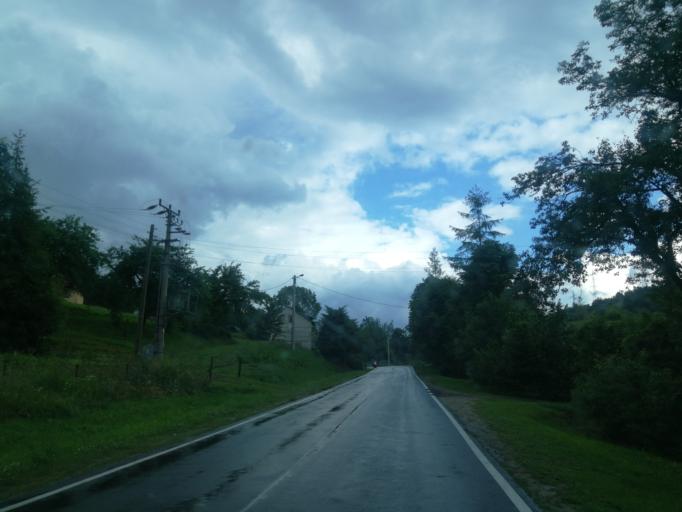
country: PL
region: Subcarpathian Voivodeship
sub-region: Powiat leski
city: Polanczyk
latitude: 49.4197
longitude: 22.4489
